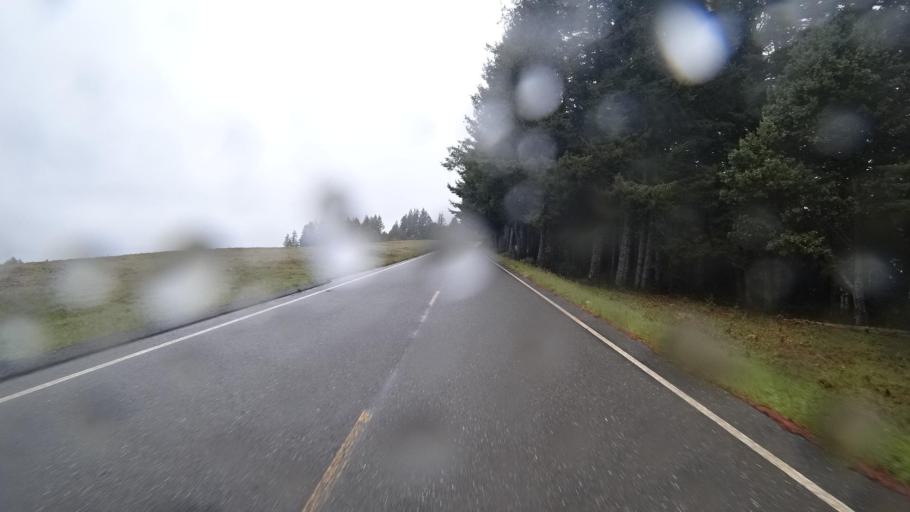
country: US
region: California
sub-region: Humboldt County
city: Westhaven-Moonstone
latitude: 41.1937
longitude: -123.9397
